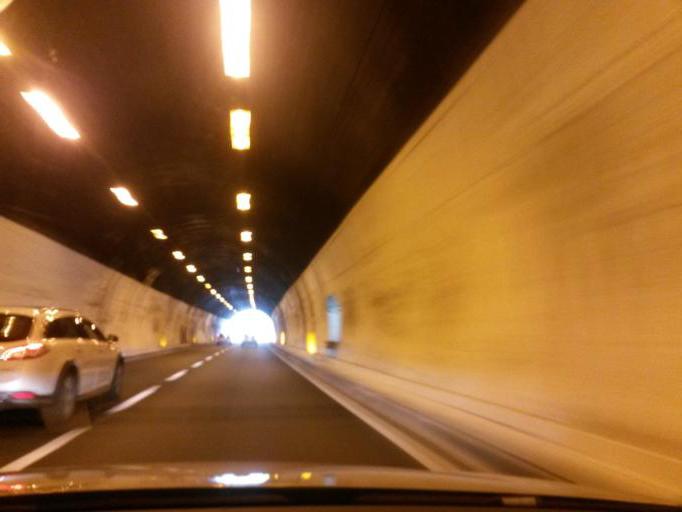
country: IT
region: Liguria
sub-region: Provincia di Genova
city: Moneglia
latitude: 44.2548
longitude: 9.4985
